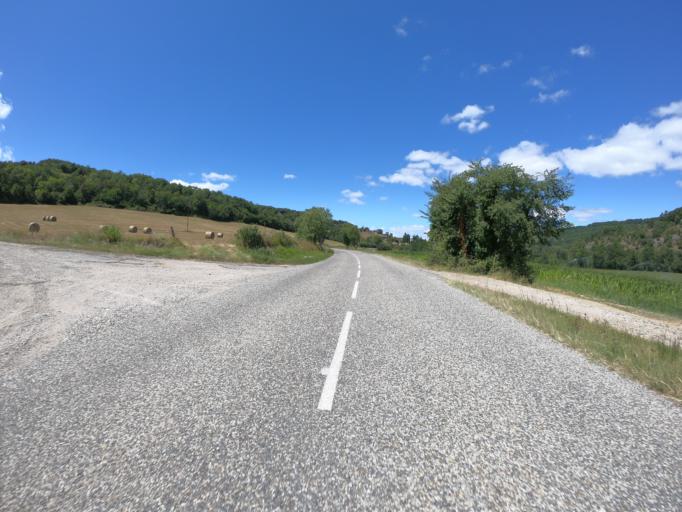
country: FR
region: Midi-Pyrenees
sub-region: Departement de l'Ariege
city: Mirepoix
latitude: 43.0467
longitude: 1.7629
